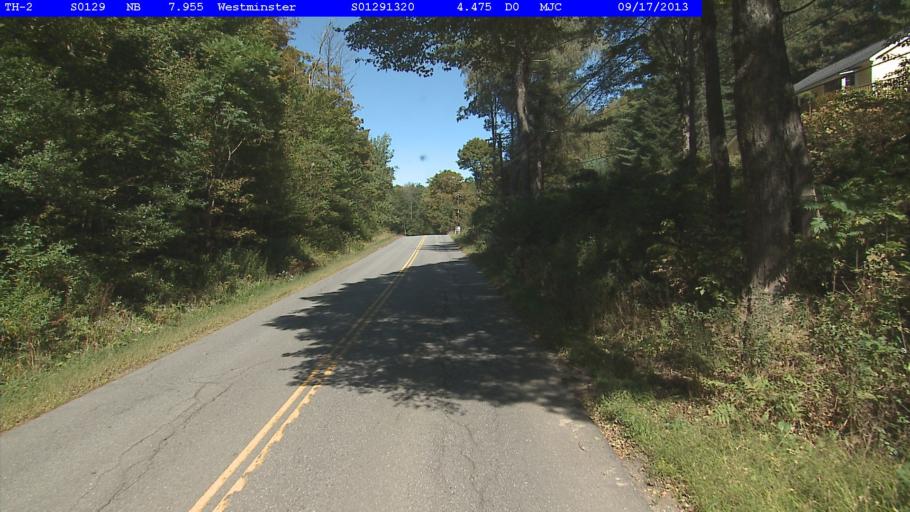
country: US
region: Vermont
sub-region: Windham County
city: Bellows Falls
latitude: 43.0795
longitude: -72.5364
